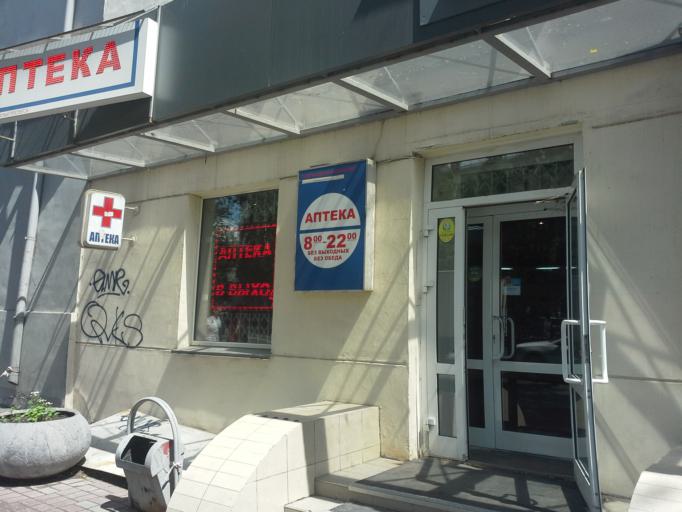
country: RU
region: Novosibirsk
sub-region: Novosibirskiy Rayon
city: Novosibirsk
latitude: 55.0241
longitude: 82.9225
